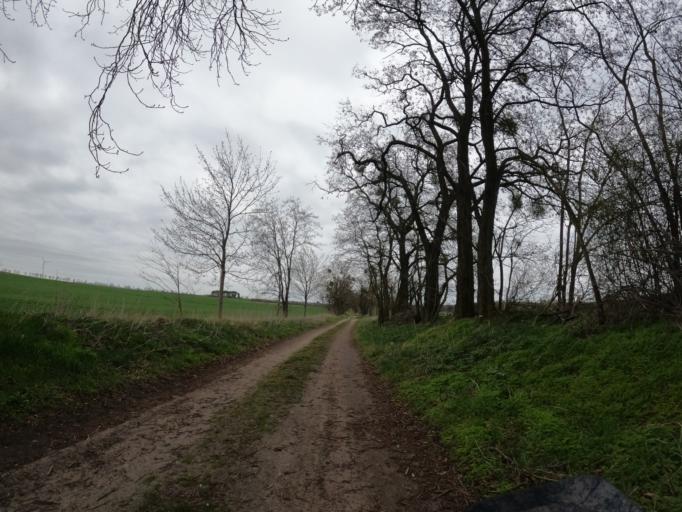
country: DE
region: Brandenburg
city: Werftpfuhl
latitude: 52.5908
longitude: 13.7985
